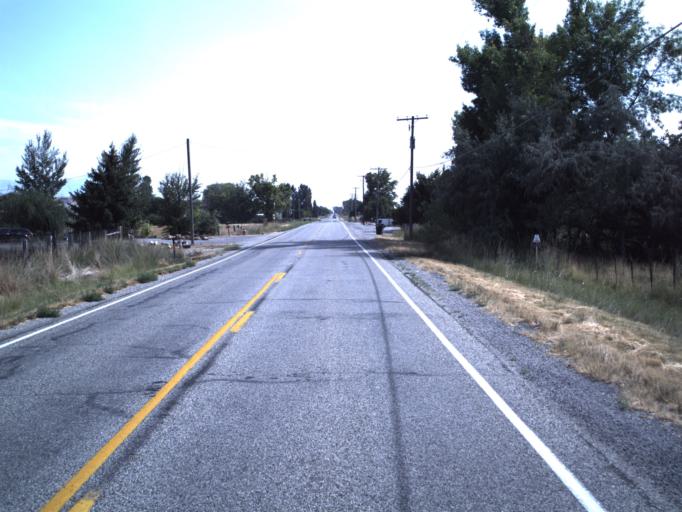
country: US
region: Utah
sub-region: Box Elder County
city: Elwood
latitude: 41.6925
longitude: -112.0900
